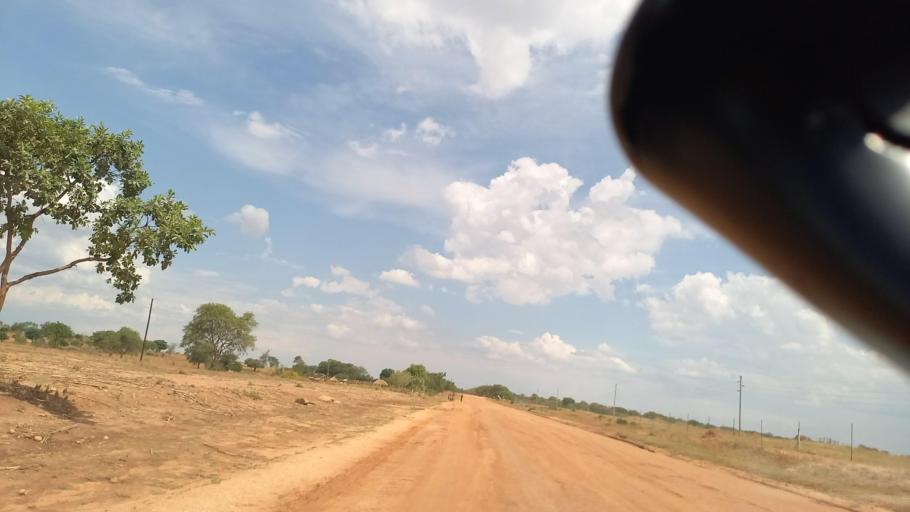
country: ZM
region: Lusaka
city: Kafue
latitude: -16.1132
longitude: 28.0303
